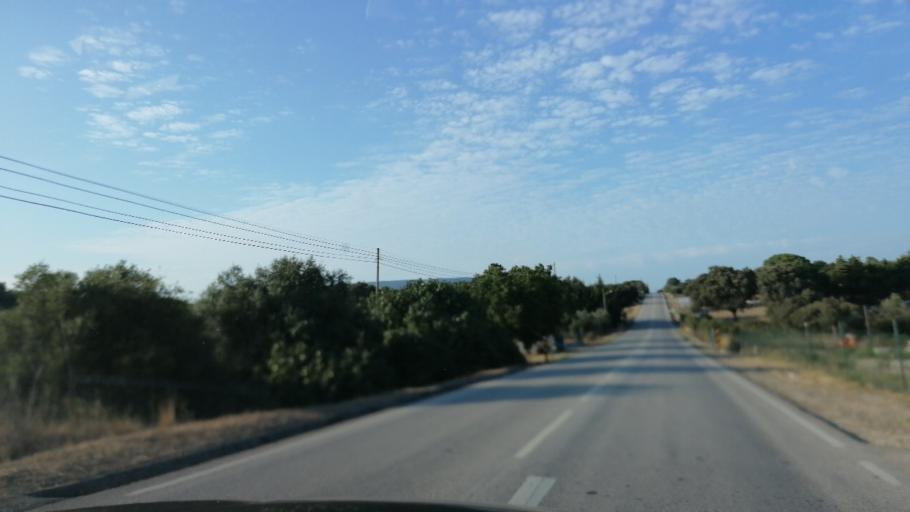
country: PT
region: Santarem
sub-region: Alcanena
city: Alcanena
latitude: 39.4405
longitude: -8.6251
